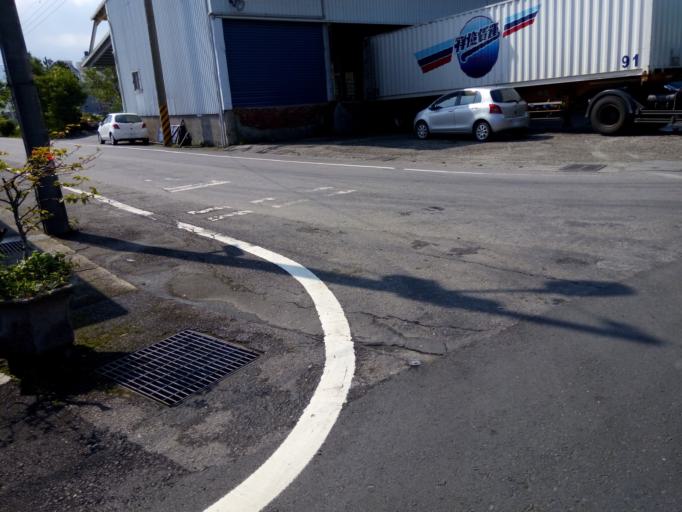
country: TW
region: Taiwan
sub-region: Yilan
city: Yilan
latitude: 24.6721
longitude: 121.7791
